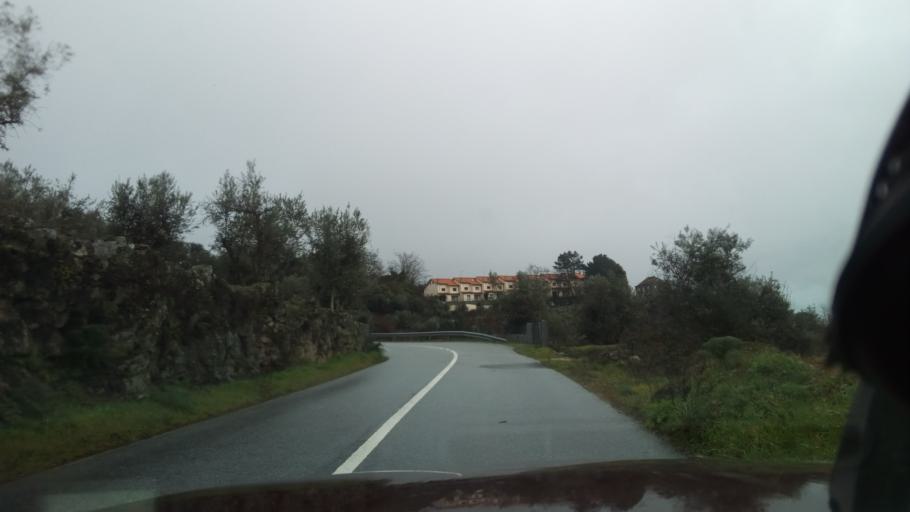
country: PT
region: Guarda
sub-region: Fornos de Algodres
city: Fornos de Algodres
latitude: 40.6288
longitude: -7.5373
